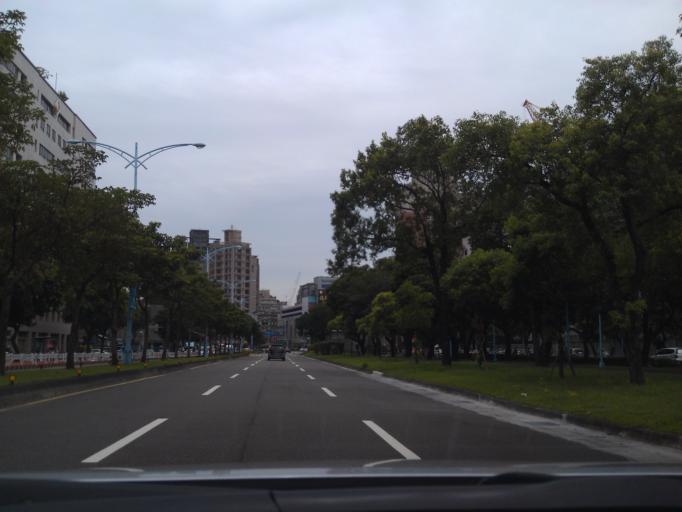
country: TW
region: Taipei
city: Taipei
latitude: 25.0362
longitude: 121.5094
